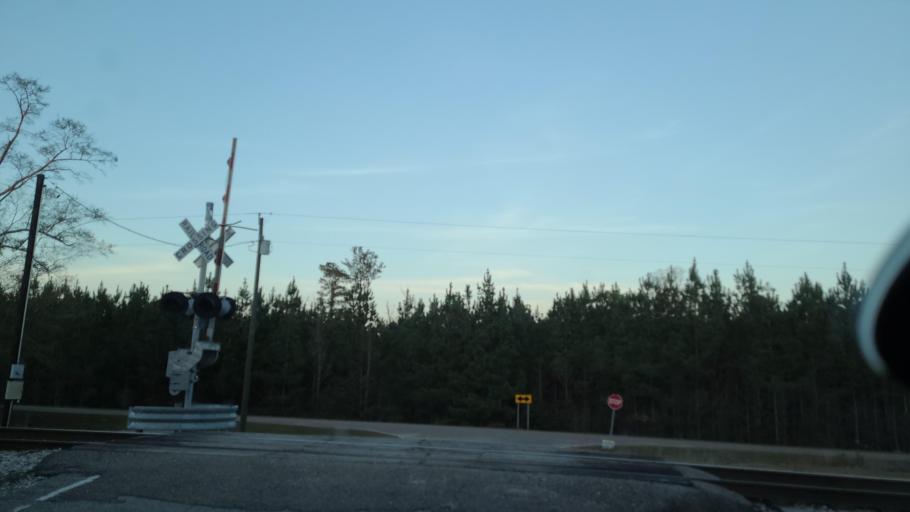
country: US
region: Mississippi
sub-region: Perry County
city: New Augusta
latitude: 31.1373
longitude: -89.2005
